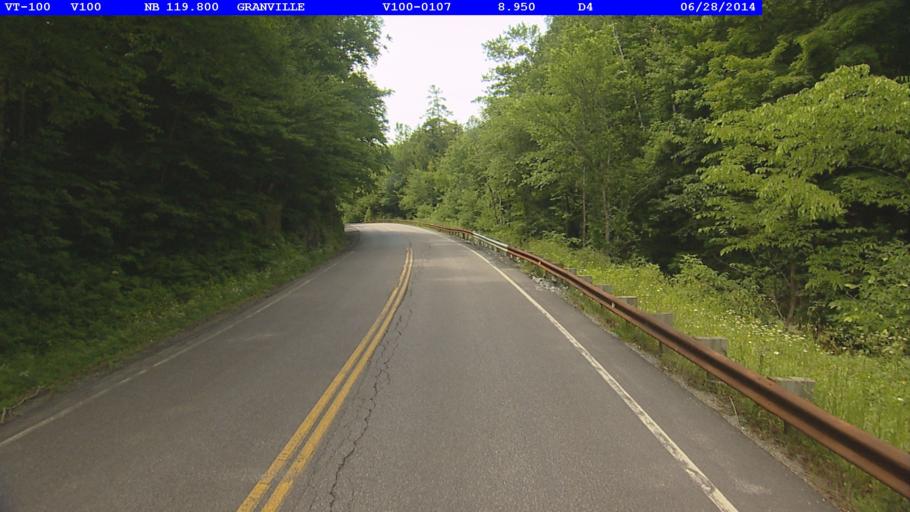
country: US
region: Vermont
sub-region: Washington County
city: Northfield
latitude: 44.0566
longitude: -72.8390
